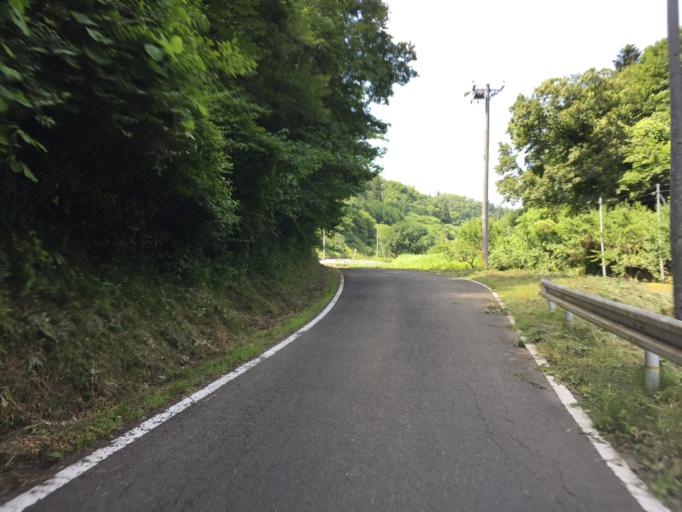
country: JP
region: Fukushima
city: Yanagawamachi-saiwaicho
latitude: 37.7640
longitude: 140.6519
